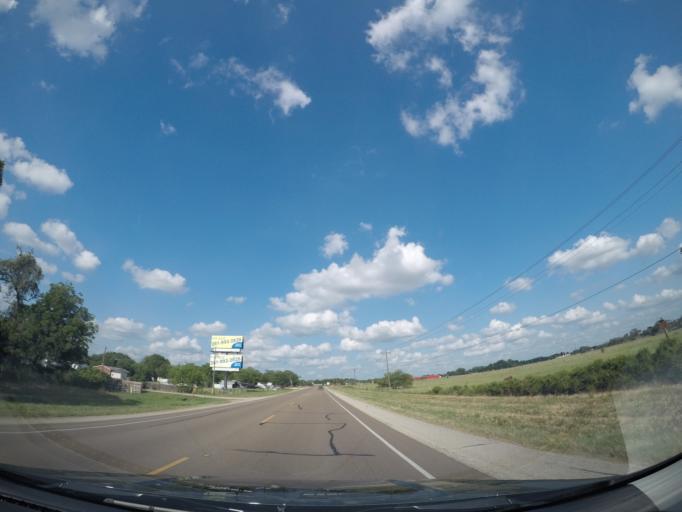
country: US
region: Texas
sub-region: Lavaca County
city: Hallettsville
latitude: 29.4322
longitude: -96.9768
